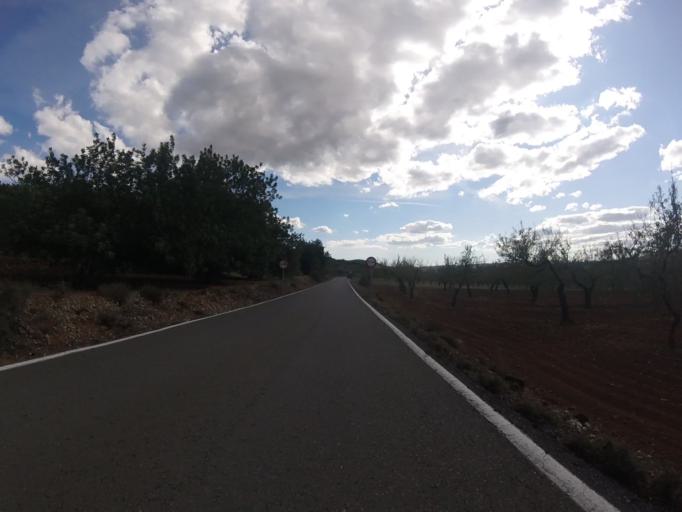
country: ES
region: Valencia
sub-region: Provincia de Castello
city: Cuevas de Vinroma
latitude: 40.3611
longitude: 0.1244
